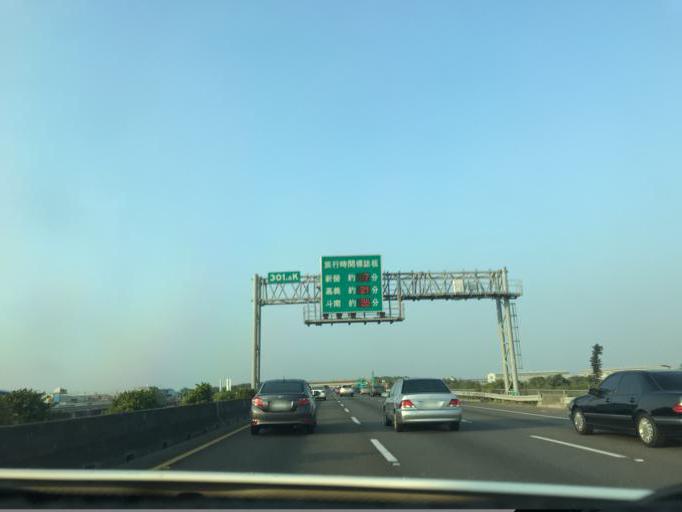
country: TW
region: Taiwan
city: Xinying
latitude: 23.2003
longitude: 120.2365
